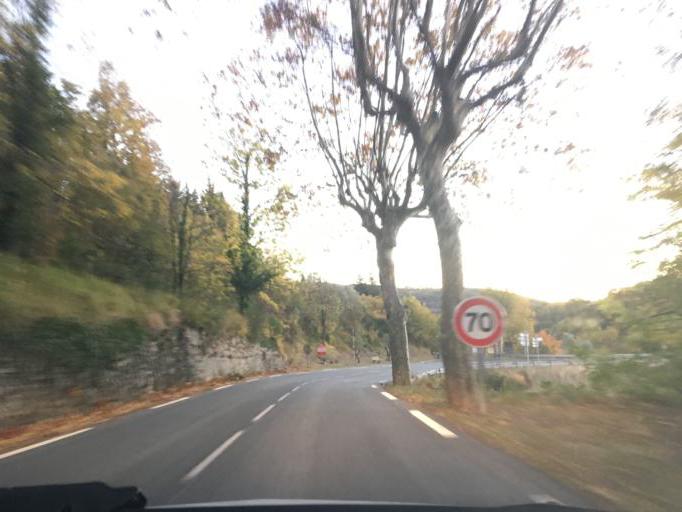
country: FR
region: Provence-Alpes-Cote d'Azur
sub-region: Departement du Var
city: Montferrat
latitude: 43.6172
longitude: 6.4805
